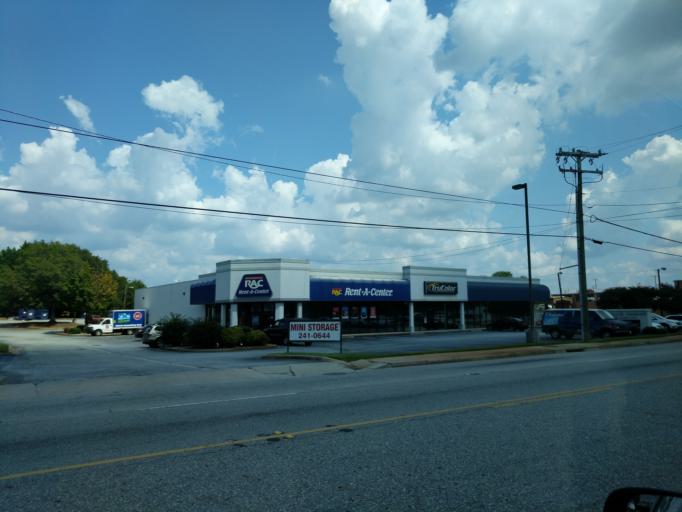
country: US
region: South Carolina
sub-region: Greenville County
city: Greenville
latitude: 34.8364
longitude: -82.3545
